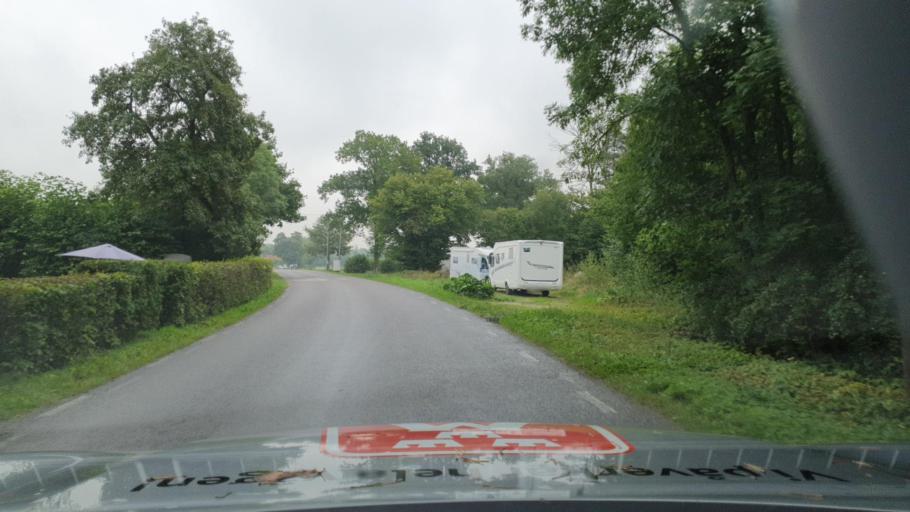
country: SE
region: Gotland
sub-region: Gotland
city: Visby
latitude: 57.7487
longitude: 18.4995
